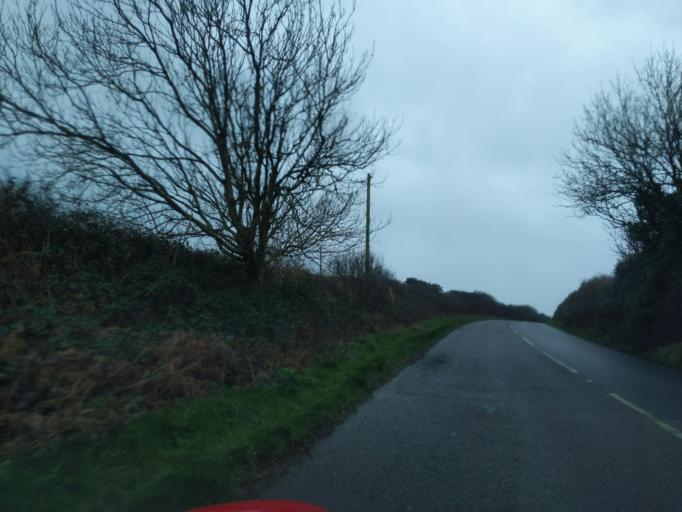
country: GB
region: England
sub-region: Cornwall
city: Saltash
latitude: 50.3613
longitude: -4.2678
